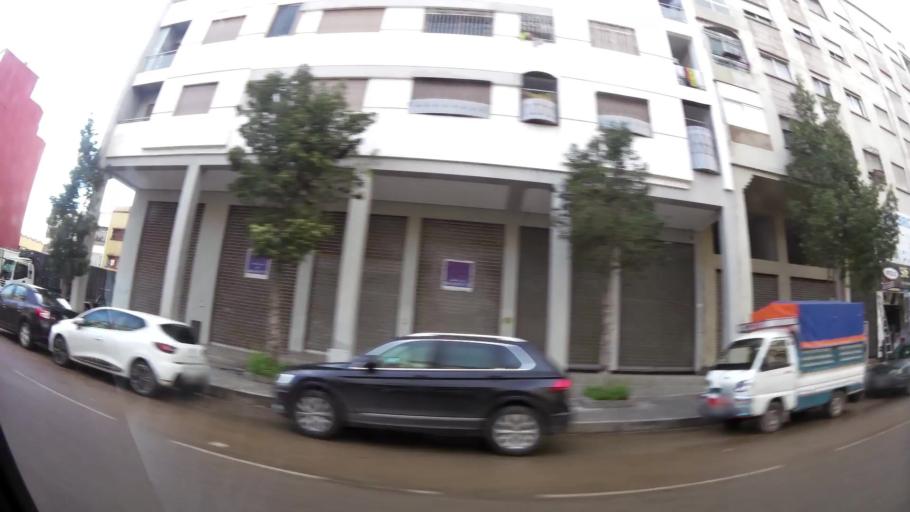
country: MA
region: Grand Casablanca
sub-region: Mediouna
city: Tit Mellil
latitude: 33.5827
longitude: -7.5246
